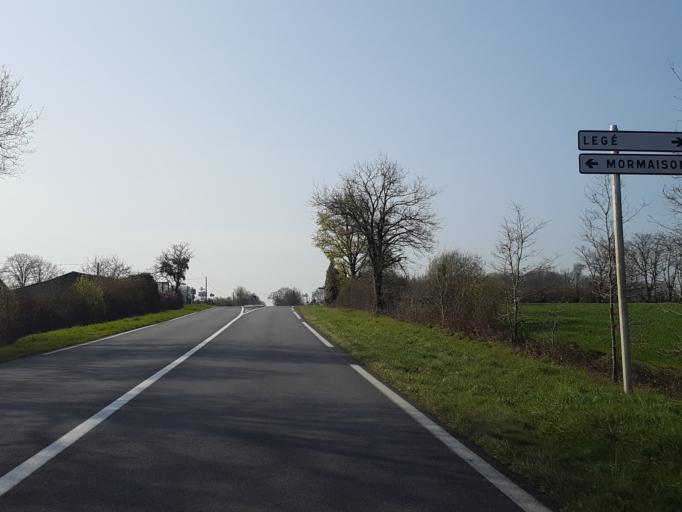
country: FR
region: Pays de la Loire
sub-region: Departement de la Vendee
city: Rocheserviere
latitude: 46.8929
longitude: -1.5019
